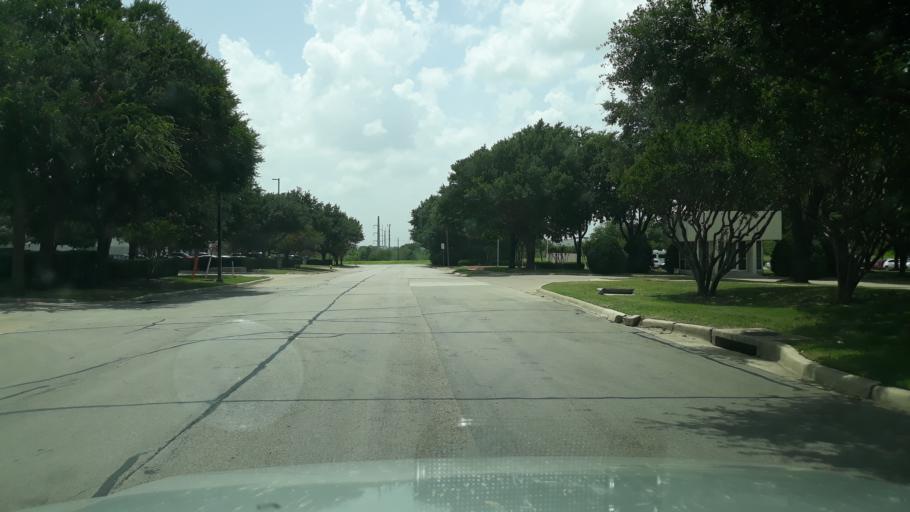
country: US
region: Texas
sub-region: Dallas County
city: Coppell
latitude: 32.9437
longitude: -97.0062
